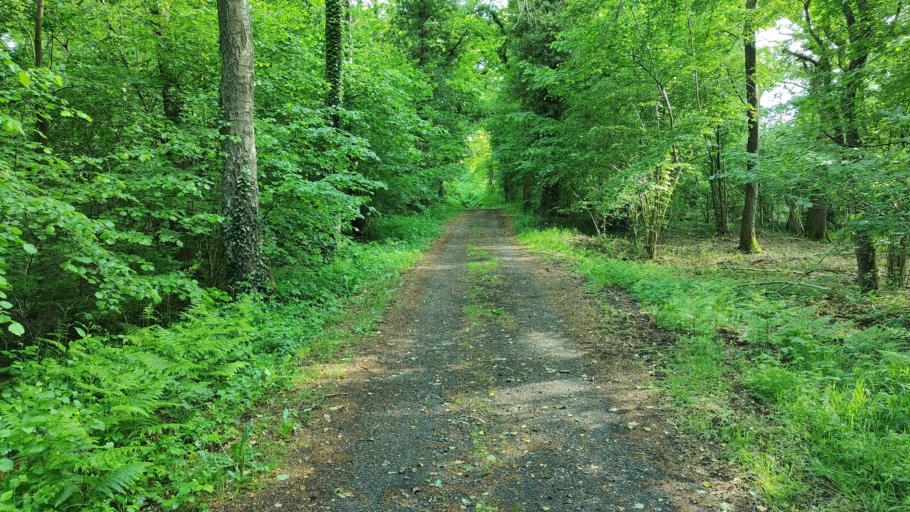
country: BE
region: Wallonia
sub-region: Province de Liege
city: La Calamine
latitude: 50.7067
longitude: 6.0472
